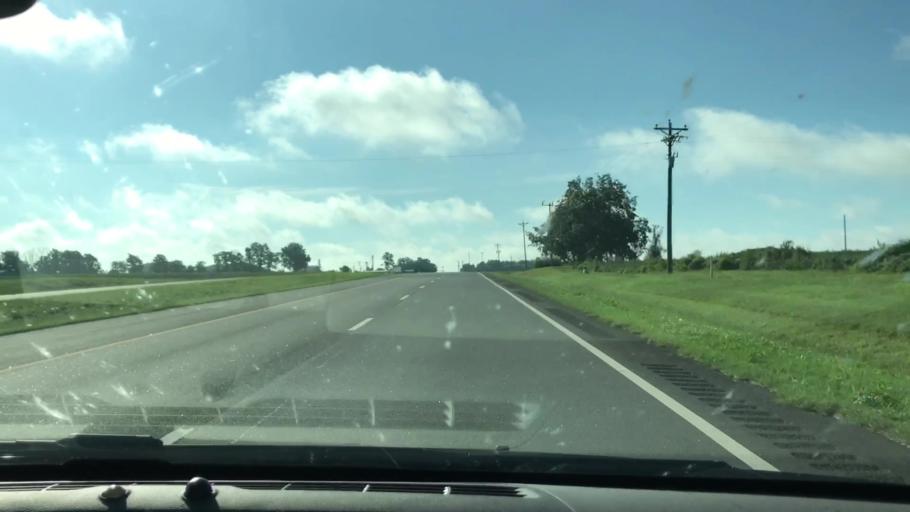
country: US
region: Georgia
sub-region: Terrell County
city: Dawson
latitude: 31.7379
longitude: -84.4070
